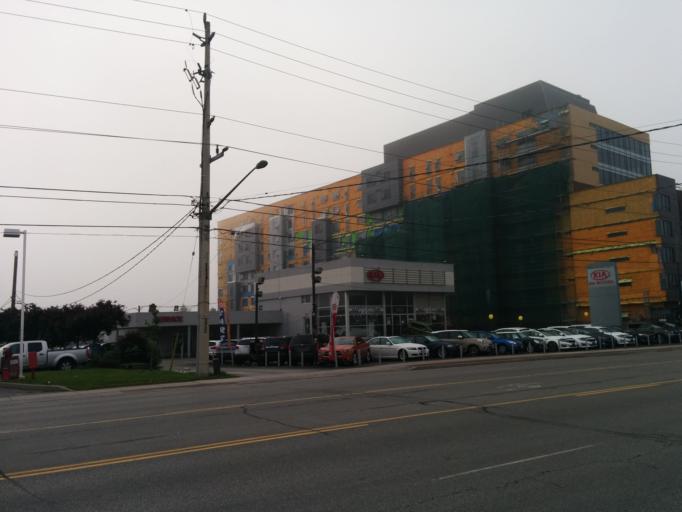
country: CA
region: Ontario
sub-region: York
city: Richmond Hill
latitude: 43.8821
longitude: -79.4399
